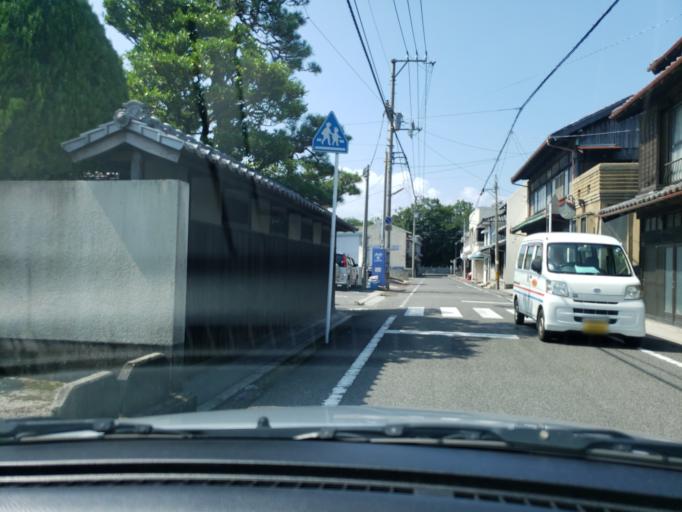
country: JP
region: Ehime
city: Hojo
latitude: 34.1071
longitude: 132.9674
